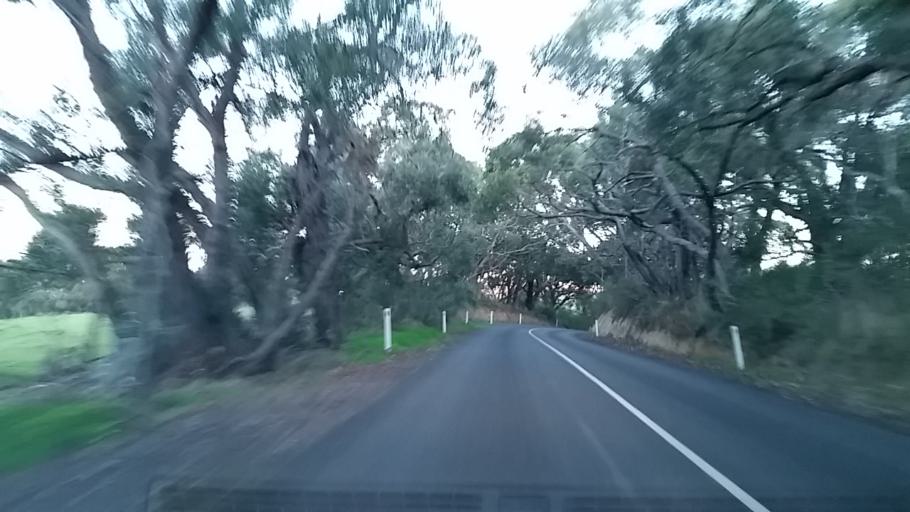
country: AU
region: South Australia
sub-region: Alexandrina
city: Mount Compass
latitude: -35.3100
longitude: 138.6172
